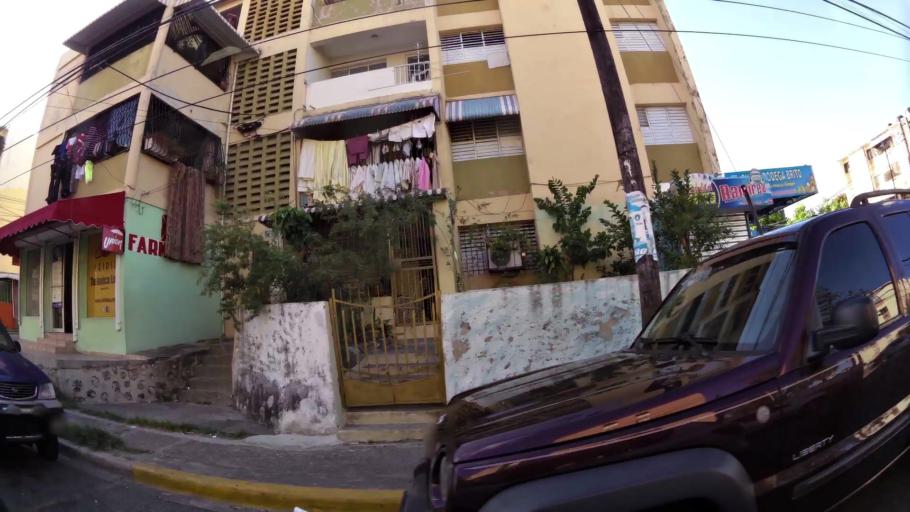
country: DO
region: Nacional
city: Santo Domingo
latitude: 18.4963
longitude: -69.9664
